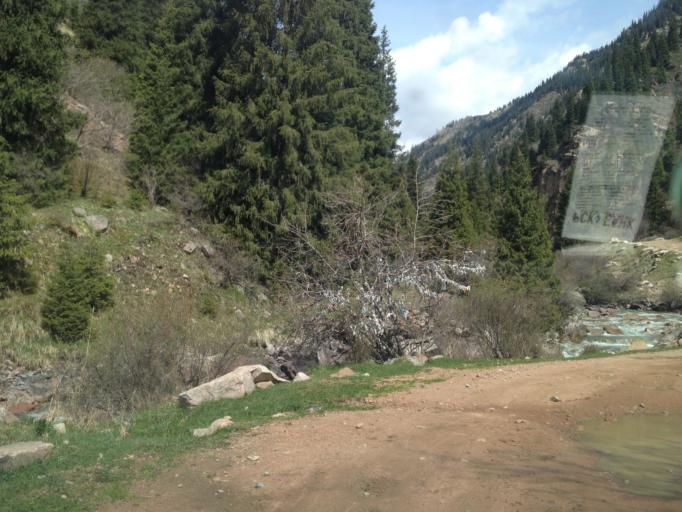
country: KG
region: Ysyk-Koel
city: Cholpon-Ata
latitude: 42.7816
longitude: 77.4701
